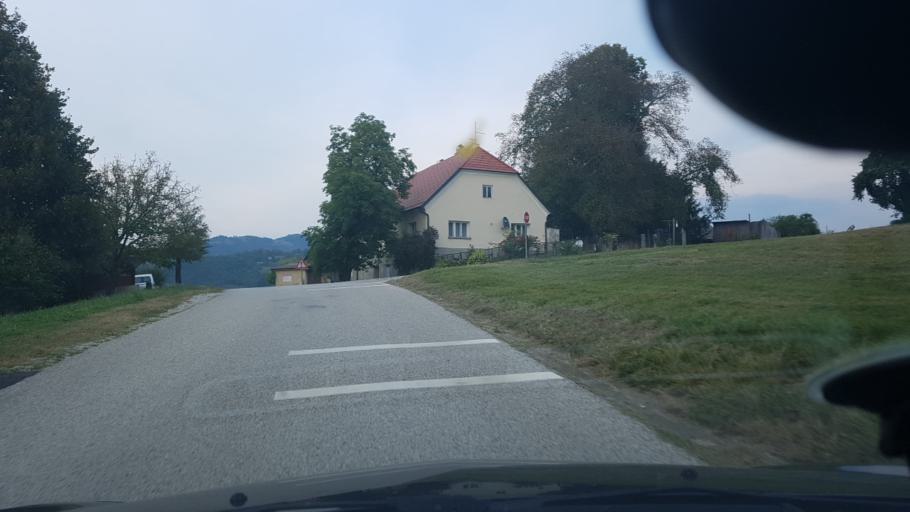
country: SI
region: Krsko
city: Senovo
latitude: 46.0290
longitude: 15.5112
